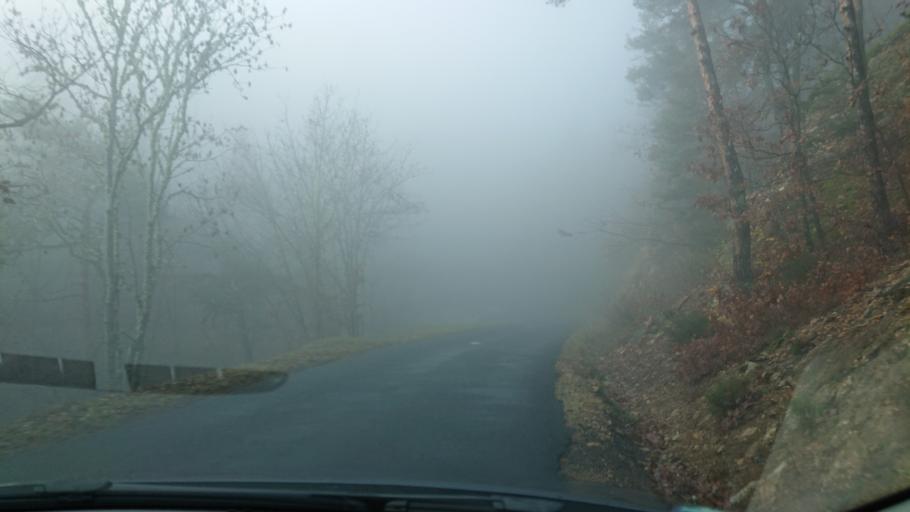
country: FR
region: Auvergne
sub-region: Departement de la Haute-Loire
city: Vorey
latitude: 45.2076
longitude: 3.9189
